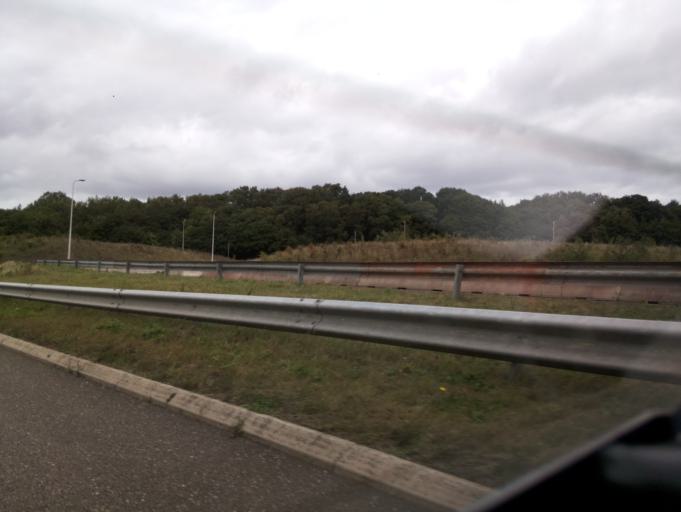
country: GB
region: England
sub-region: Devon
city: Kingskerswell
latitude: 50.5113
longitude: -3.5877
